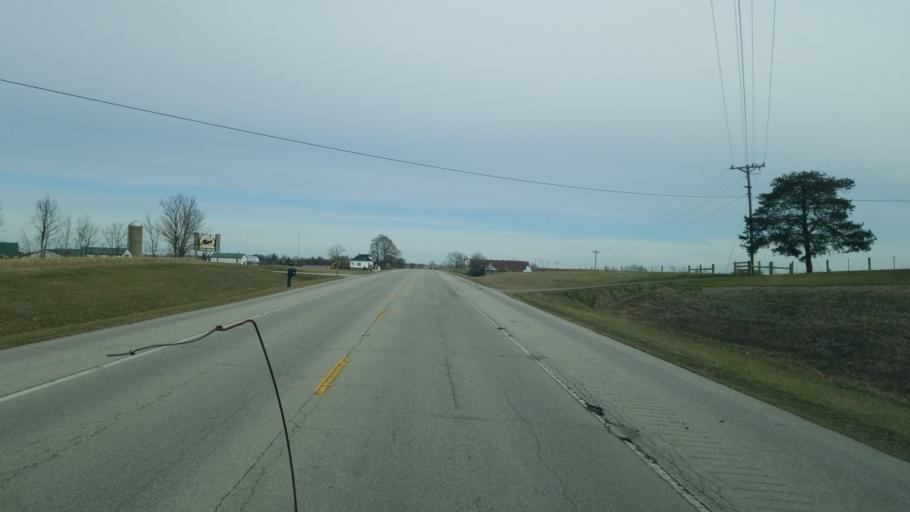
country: US
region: Kentucky
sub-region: Fleming County
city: Flemingsburg
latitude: 38.4823
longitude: -83.8704
